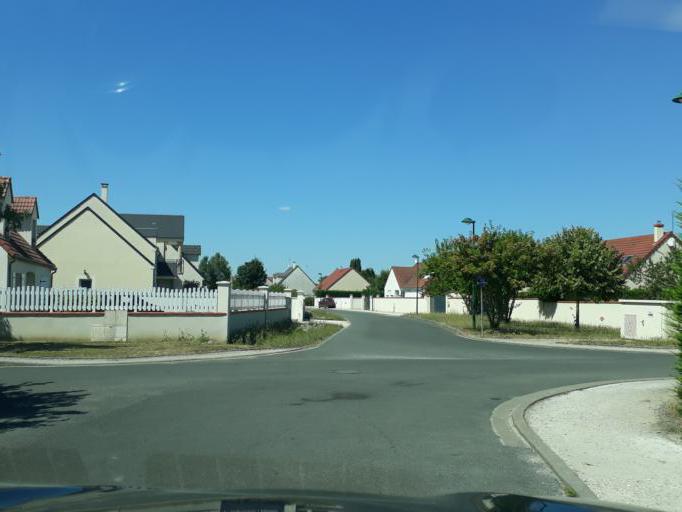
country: FR
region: Centre
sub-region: Departement du Loiret
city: Saran
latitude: 47.9864
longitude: 1.8911
